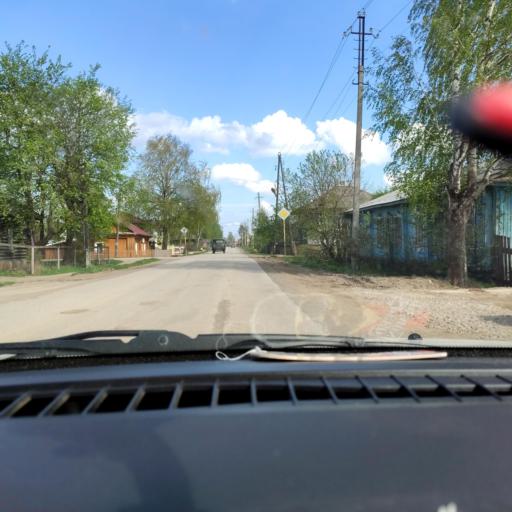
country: RU
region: Perm
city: Kudymkar
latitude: 59.0075
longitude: 54.6554
